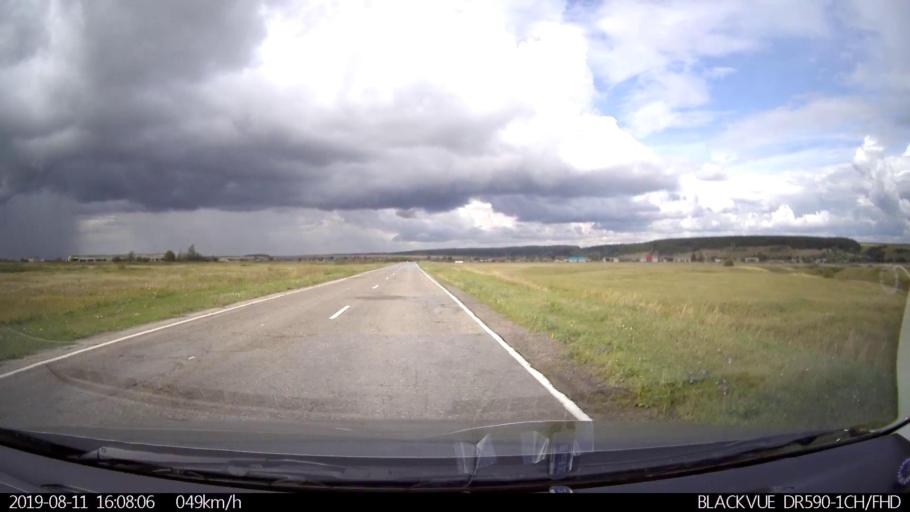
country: RU
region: Ulyanovsk
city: Ignatovka
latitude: 53.9821
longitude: 47.6474
